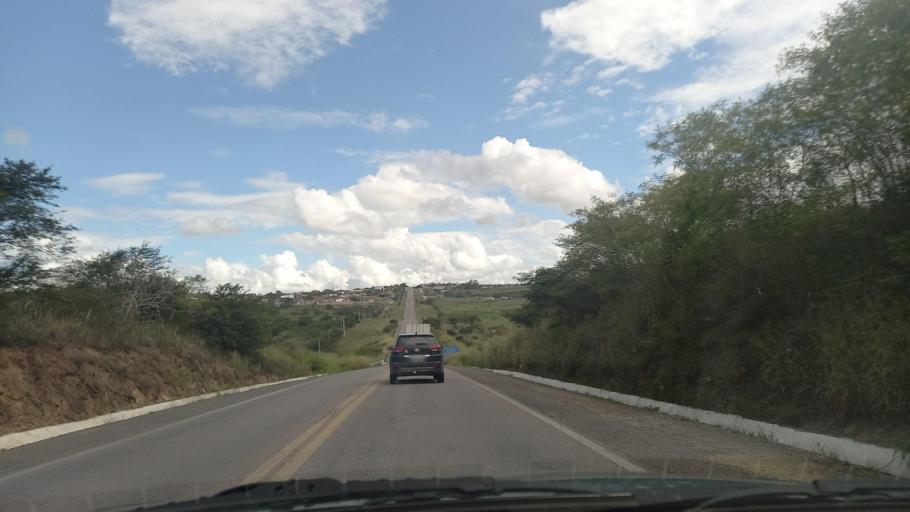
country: BR
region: Pernambuco
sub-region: Lajedo
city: Lajedo
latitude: -8.6960
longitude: -36.4132
